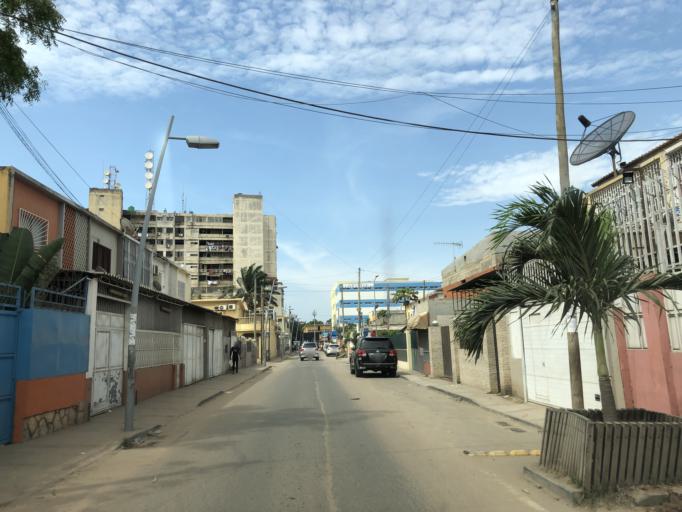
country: AO
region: Luanda
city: Luanda
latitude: -8.8210
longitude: 13.2523
